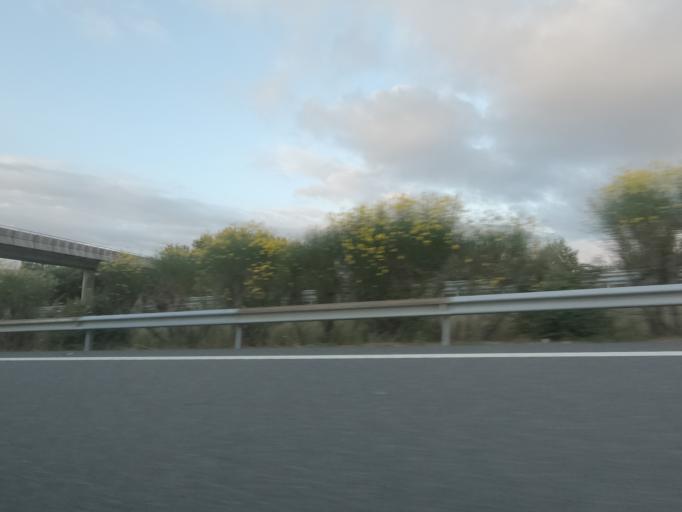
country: ES
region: Galicia
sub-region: Provincia de Pontevedra
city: Covelo
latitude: 42.1908
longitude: -8.3084
